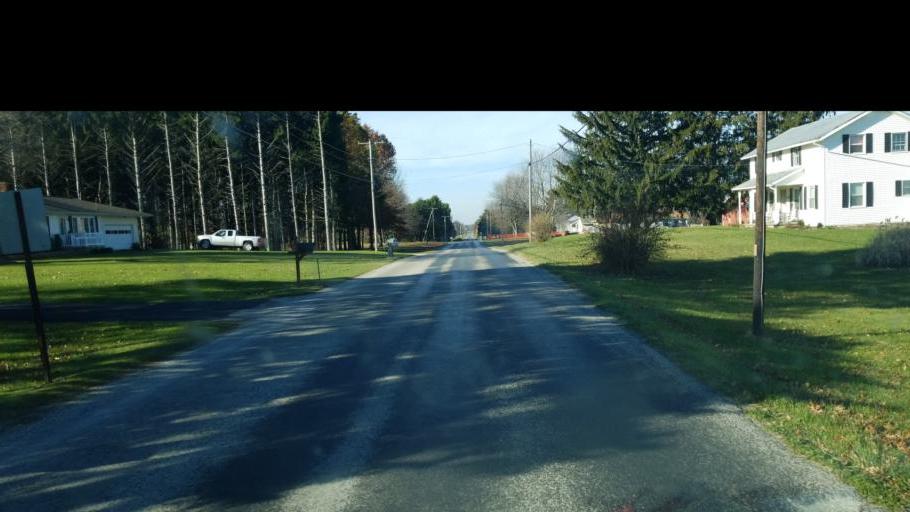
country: US
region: Ohio
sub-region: Richland County
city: Shelby
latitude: 40.8576
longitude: -82.6123
